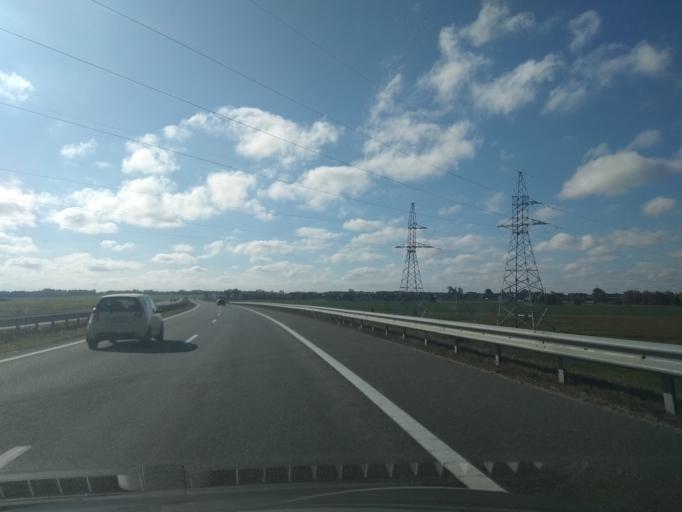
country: BY
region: Minsk
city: Stan'kava
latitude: 53.7039
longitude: 27.2150
